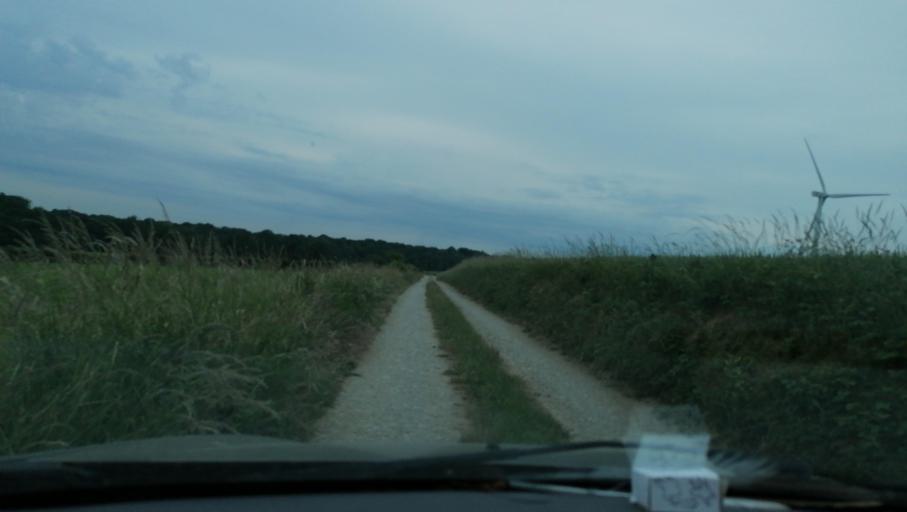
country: BE
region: Wallonia
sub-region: Province du Hainaut
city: Beaumont
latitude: 50.2077
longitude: 4.1623
